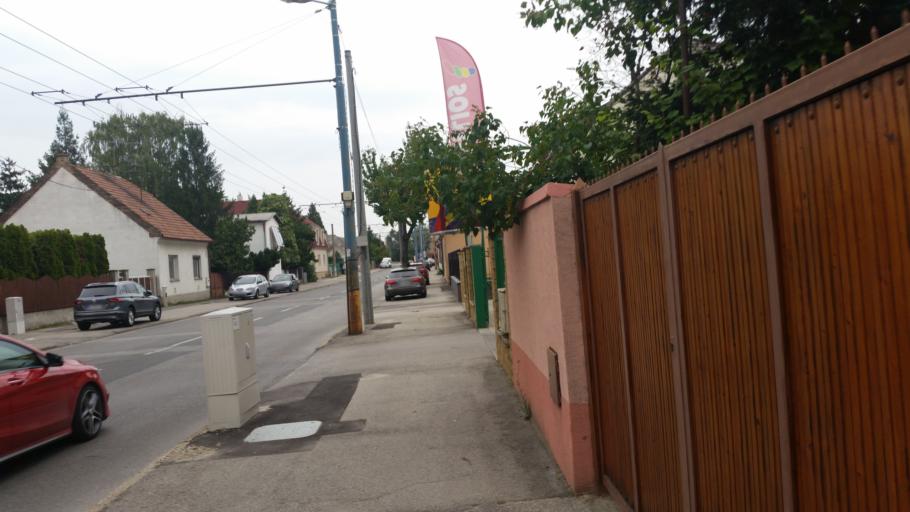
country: SK
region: Bratislavsky
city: Bratislava
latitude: 48.1467
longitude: 17.1823
